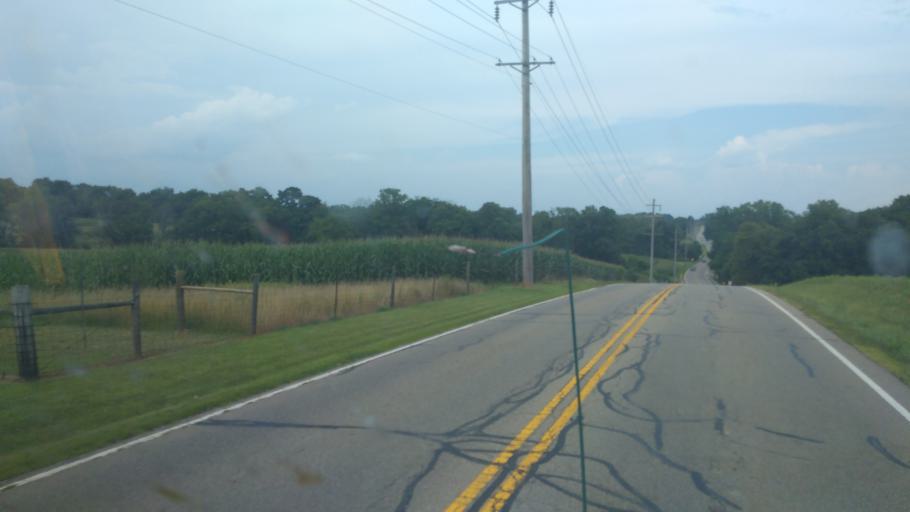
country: US
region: Ohio
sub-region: Fairfield County
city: Lancaster
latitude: 39.7685
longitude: -82.6046
